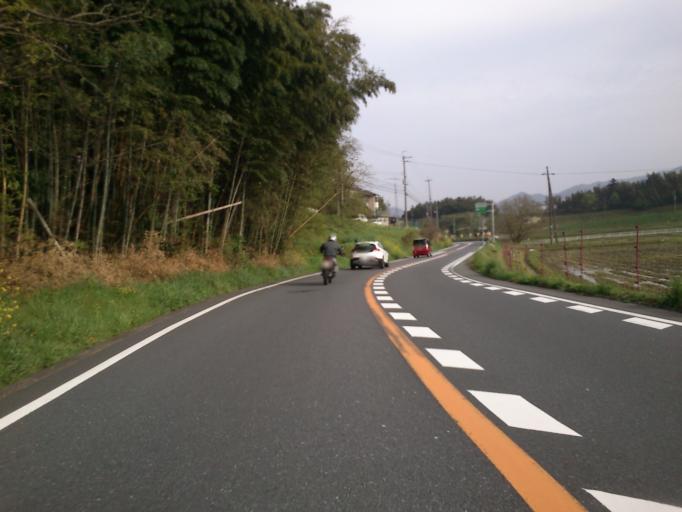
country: JP
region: Kyoto
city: Ayabe
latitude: 35.1918
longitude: 135.3619
